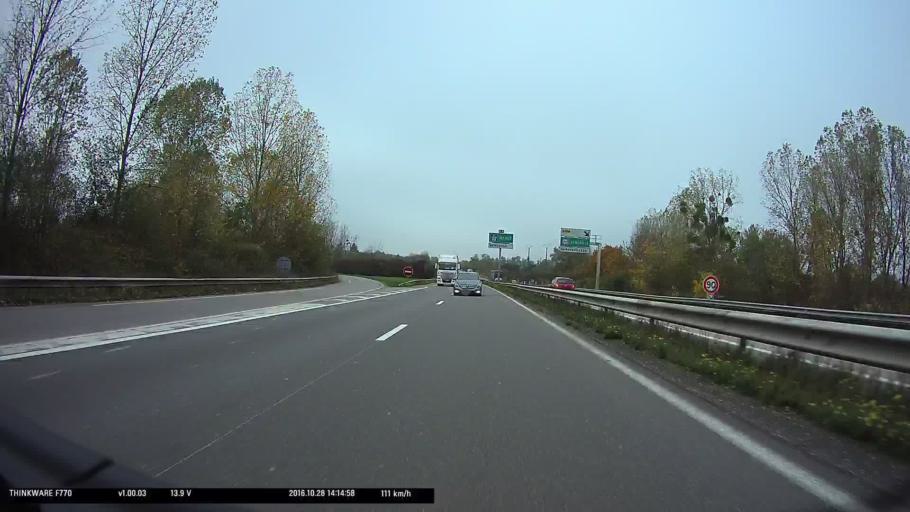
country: FR
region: Lorraine
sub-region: Departement de Meurthe-et-Moselle
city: Luneville
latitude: 48.5748
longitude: 6.4874
